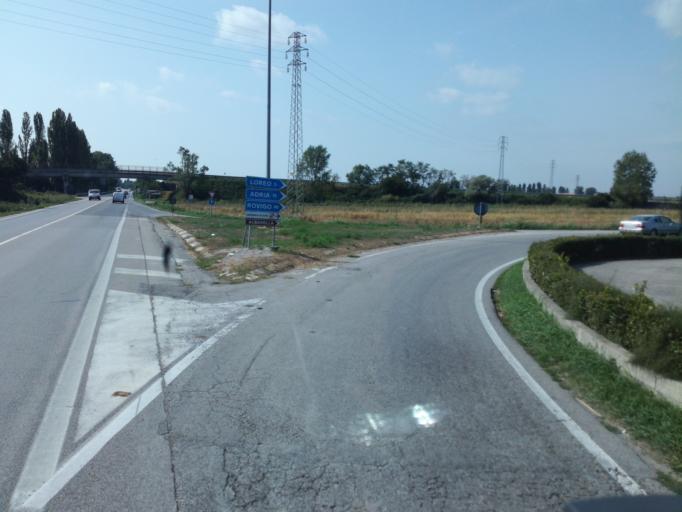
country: IT
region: Veneto
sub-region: Provincia di Rovigo
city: Rosolina
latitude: 45.0677
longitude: 12.2446
